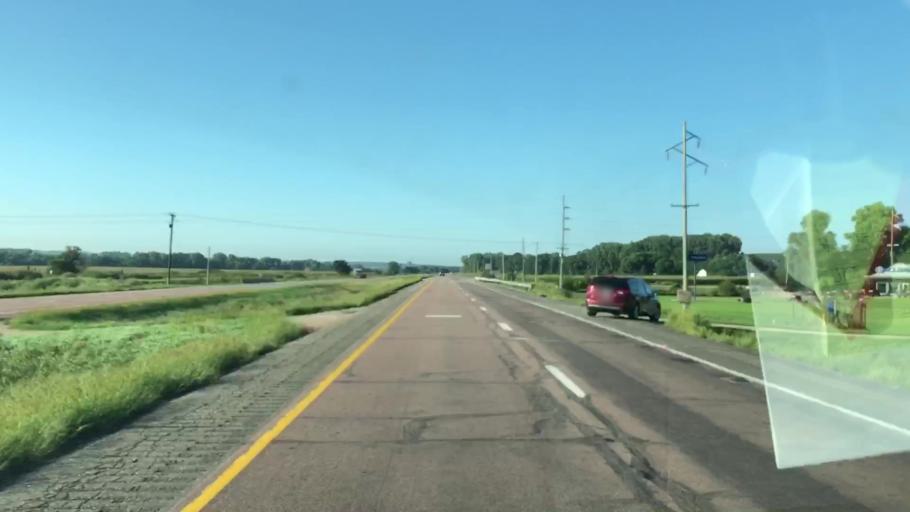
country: US
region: Iowa
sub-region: Woodbury County
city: Sioux City
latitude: 42.5954
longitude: -96.3046
